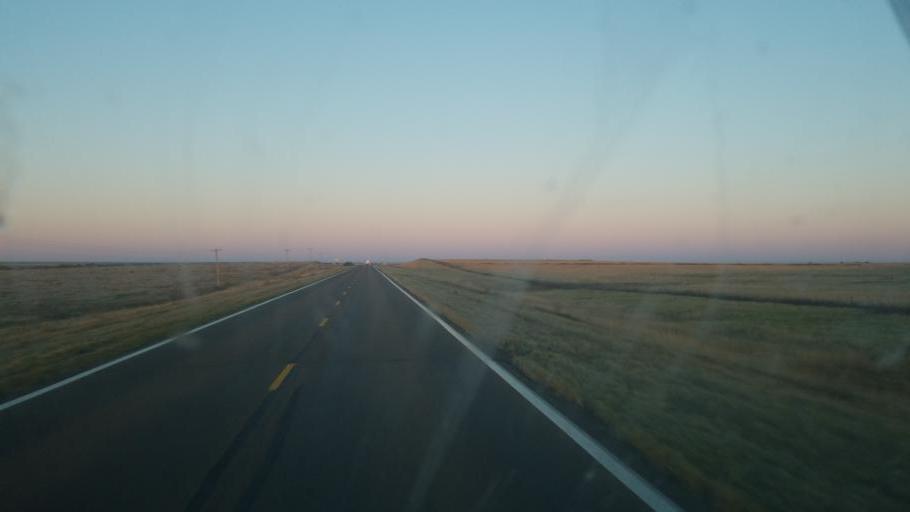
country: US
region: Kansas
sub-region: Wallace County
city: Sharon Springs
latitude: 38.9024
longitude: -101.6681
